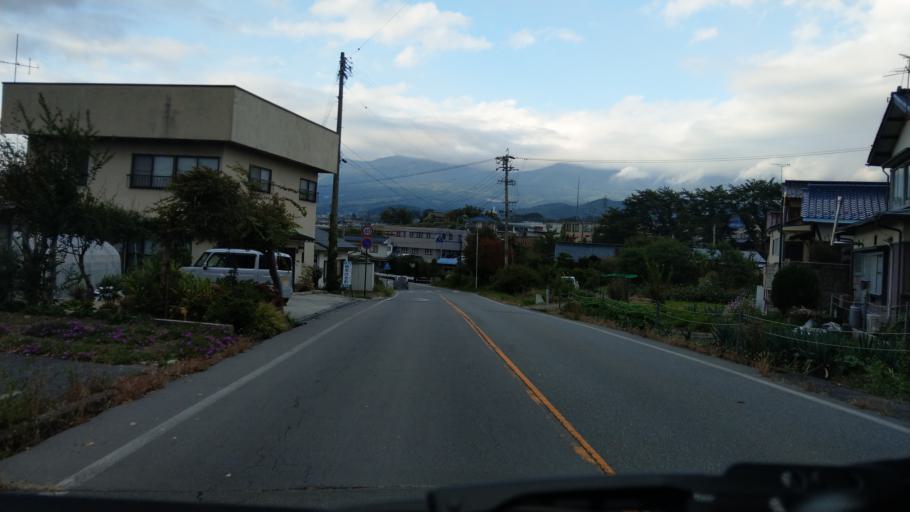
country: JP
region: Nagano
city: Komoro
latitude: 36.3158
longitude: 138.4318
